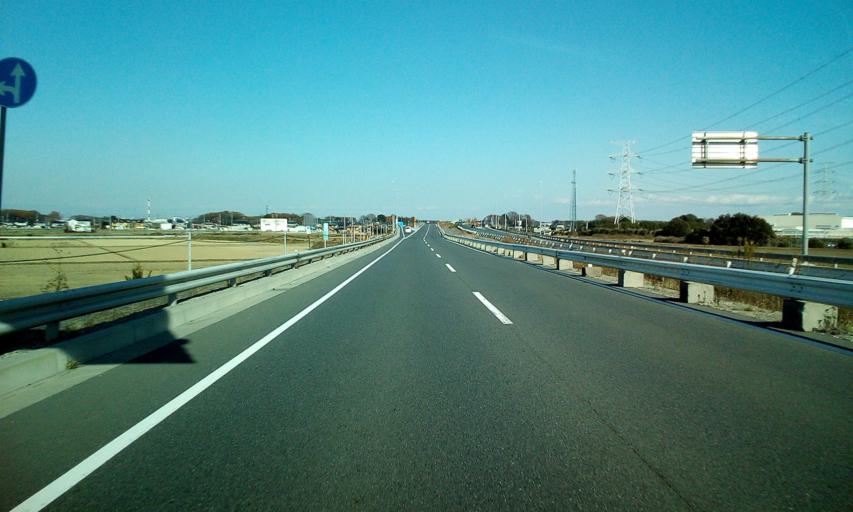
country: JP
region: Ibaraki
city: Sakai
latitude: 36.1316
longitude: 139.7628
